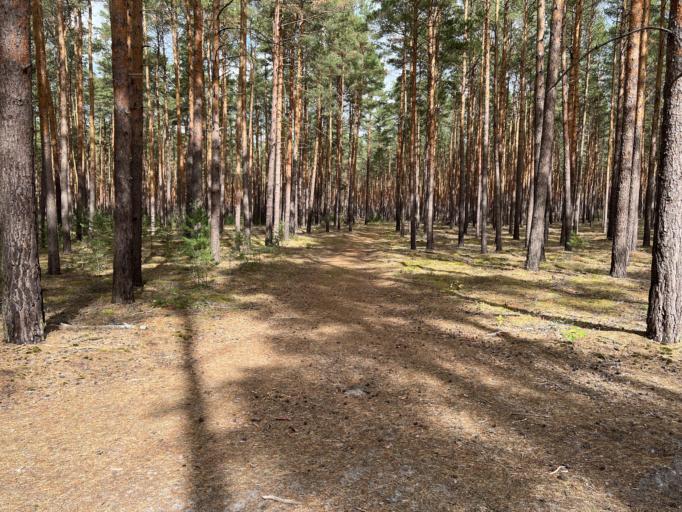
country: DE
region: Brandenburg
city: Gross Koris
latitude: 52.2205
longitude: 13.7207
